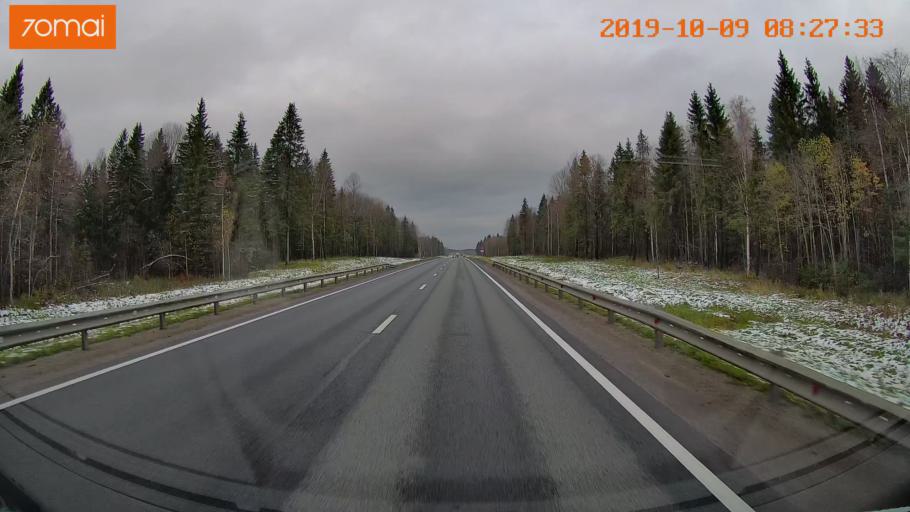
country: RU
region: Vologda
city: Gryazovets
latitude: 58.8052
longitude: 40.2469
